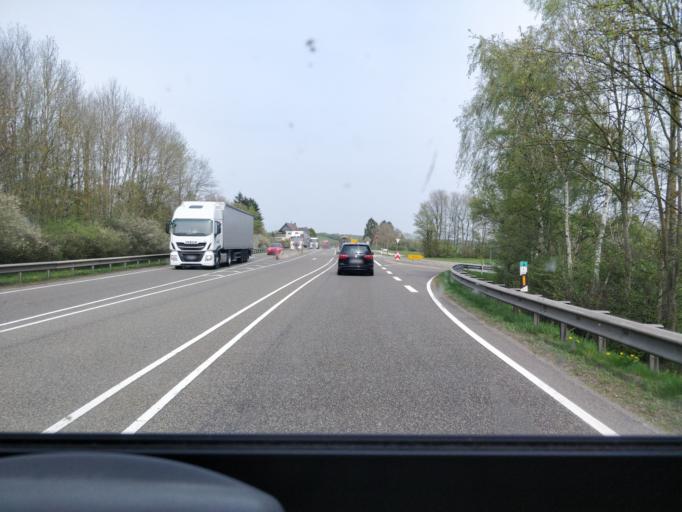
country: DE
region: North Rhine-Westphalia
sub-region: Regierungsbezirk Koln
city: Blankenheim
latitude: 50.4541
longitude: 6.6772
